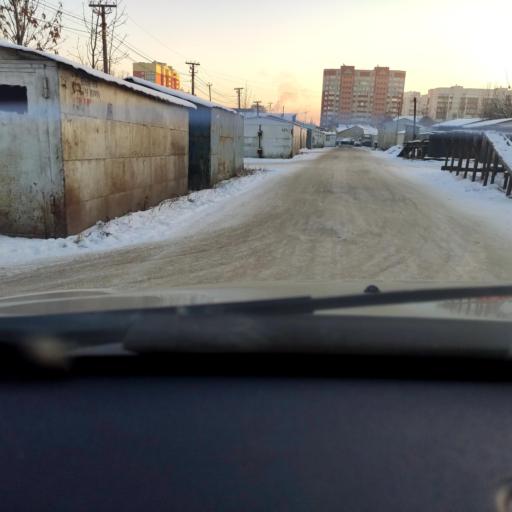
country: RU
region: Bashkortostan
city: Mikhaylovka
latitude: 54.7164
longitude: 55.8285
